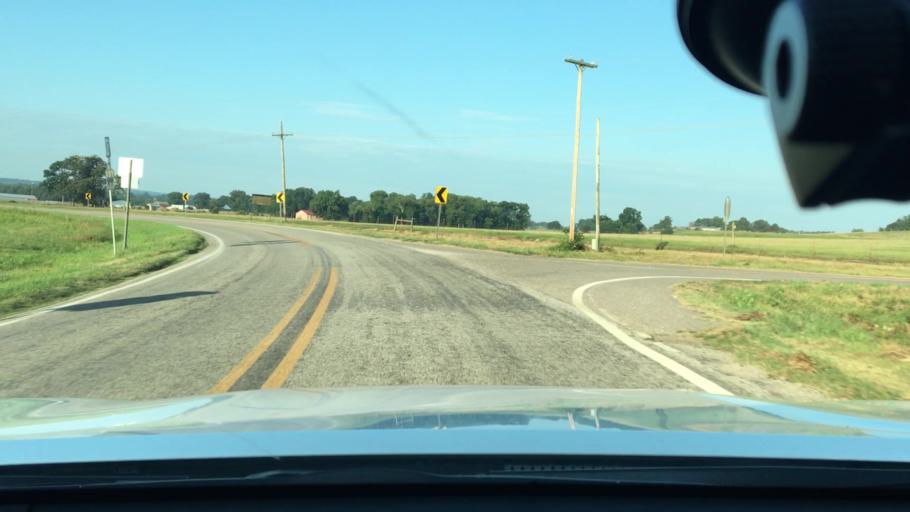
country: US
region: Arkansas
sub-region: Johnson County
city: Coal Hill
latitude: 35.3372
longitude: -93.6313
